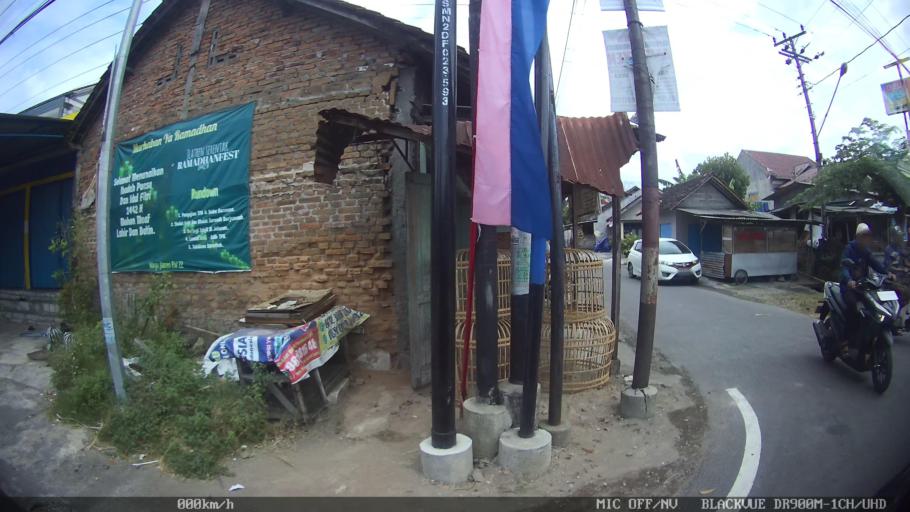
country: ID
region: Central Java
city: Candi Prambanan
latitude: -7.8101
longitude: 110.4829
